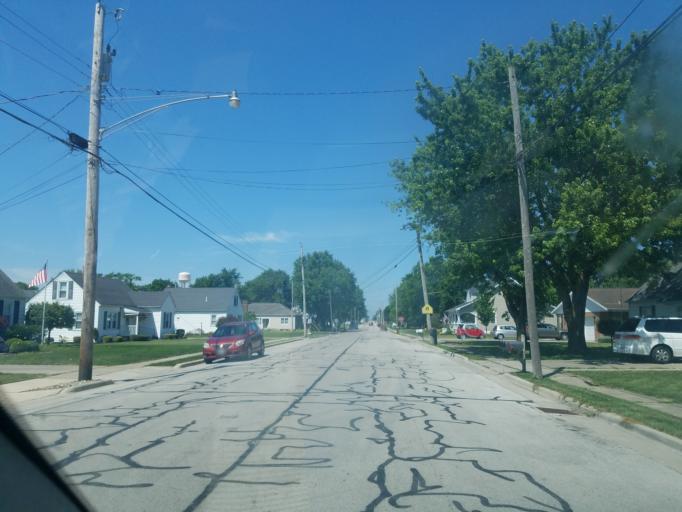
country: US
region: Ohio
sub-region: Mercer County
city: Saint Henry
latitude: 40.4214
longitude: -84.6357
